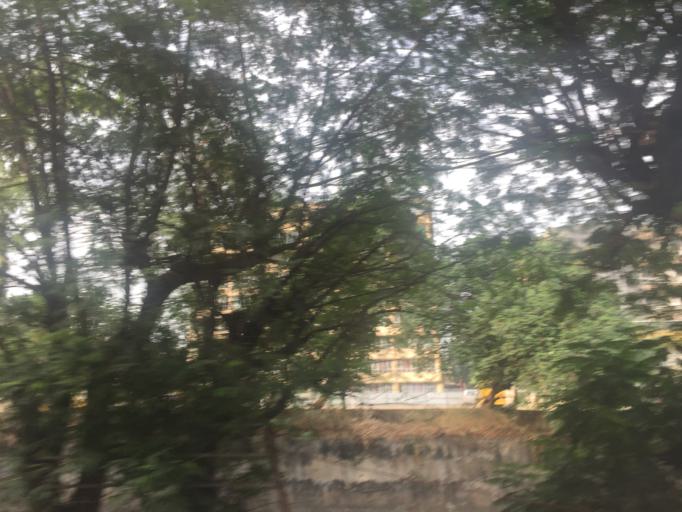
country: IN
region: Maharashtra
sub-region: Thane
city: Airoli
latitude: 19.1556
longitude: 72.9970
